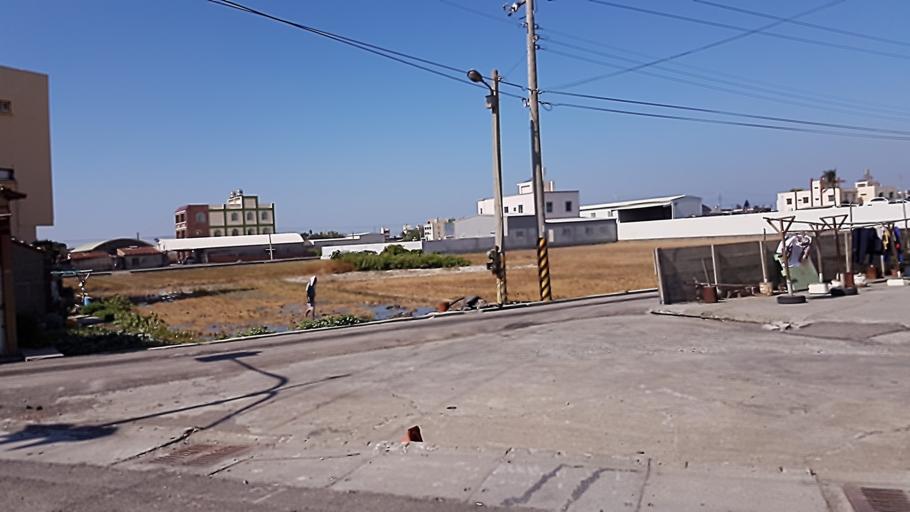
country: TW
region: Taiwan
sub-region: Changhua
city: Chang-hua
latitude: 24.0696
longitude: 120.4548
